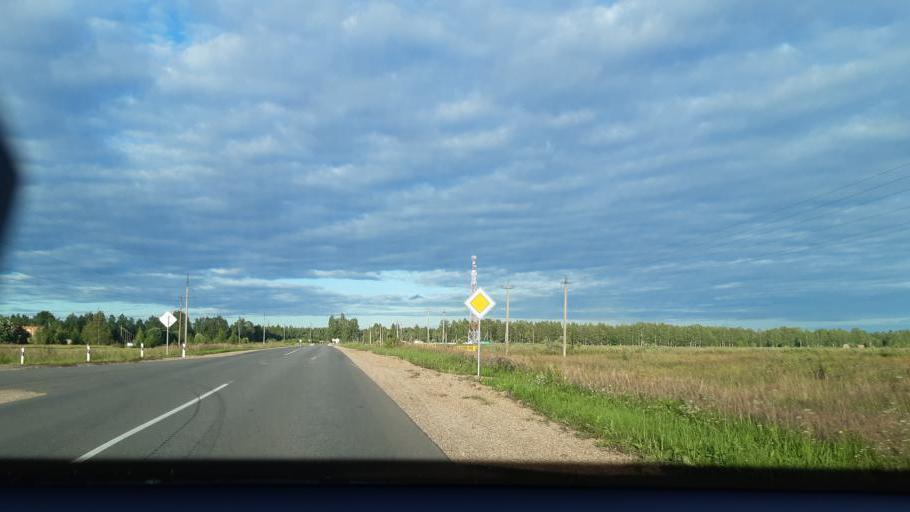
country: RU
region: Smolensk
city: Yel'nya
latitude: 54.5941
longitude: 33.1811
